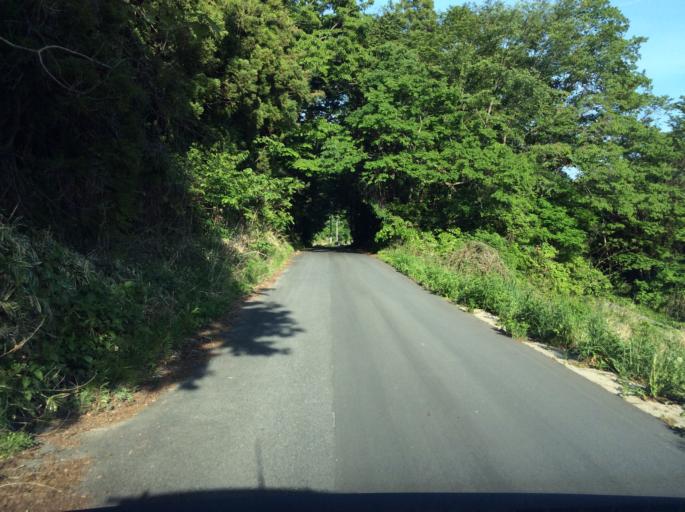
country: JP
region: Fukushima
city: Iwaki
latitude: 37.1626
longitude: 140.9906
